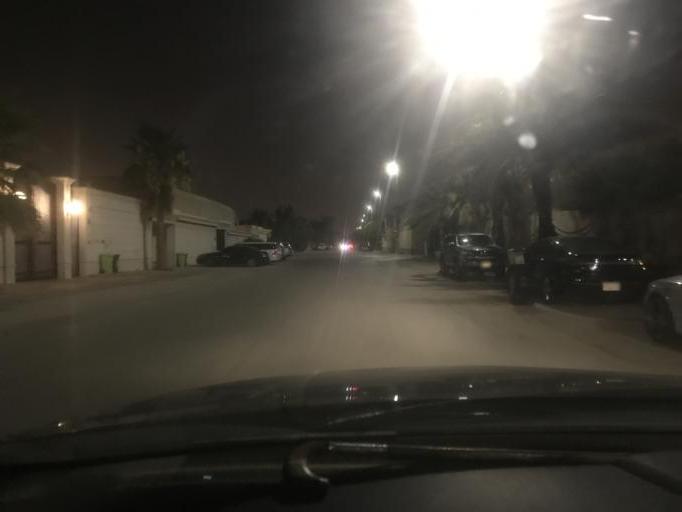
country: SA
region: Ar Riyad
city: Riyadh
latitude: 24.7309
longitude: 46.7793
